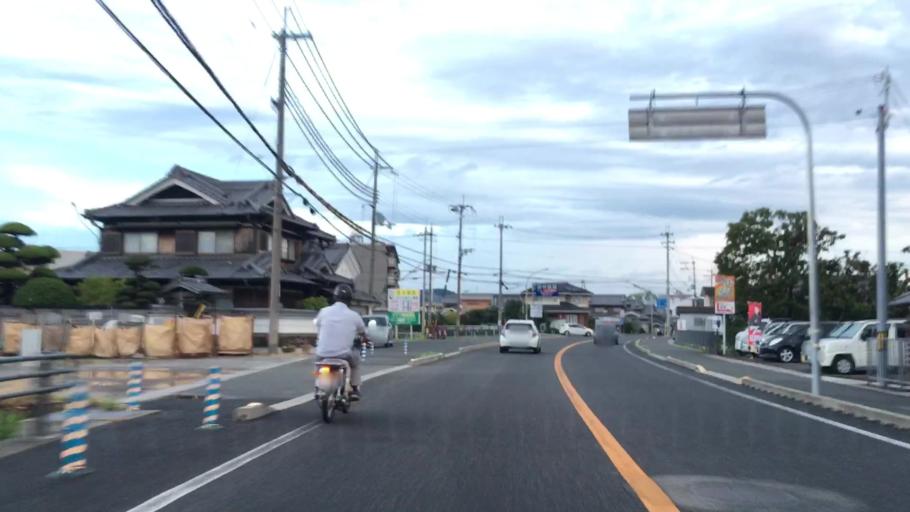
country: JP
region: Hyogo
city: Himeji
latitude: 34.9119
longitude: 134.7391
